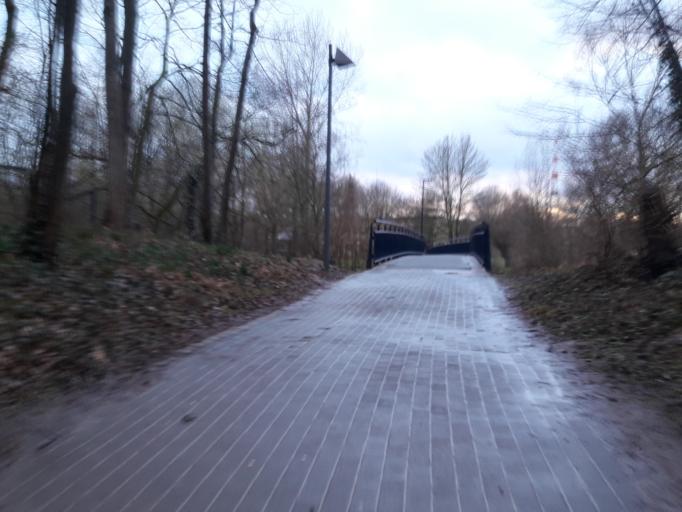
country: DE
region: North Rhine-Westphalia
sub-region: Regierungsbezirk Detmold
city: Paderborn
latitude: 51.7476
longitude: 8.7081
